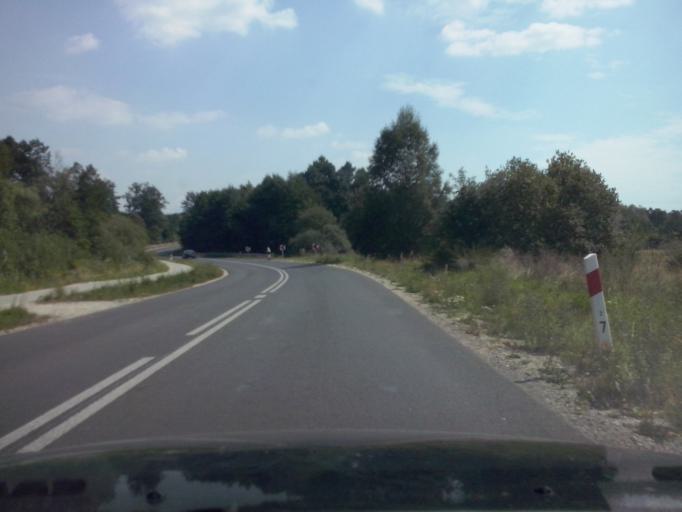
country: PL
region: Swietokrzyskie
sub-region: Powiat kielecki
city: Chmielnik
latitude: 50.6159
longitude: 20.7819
